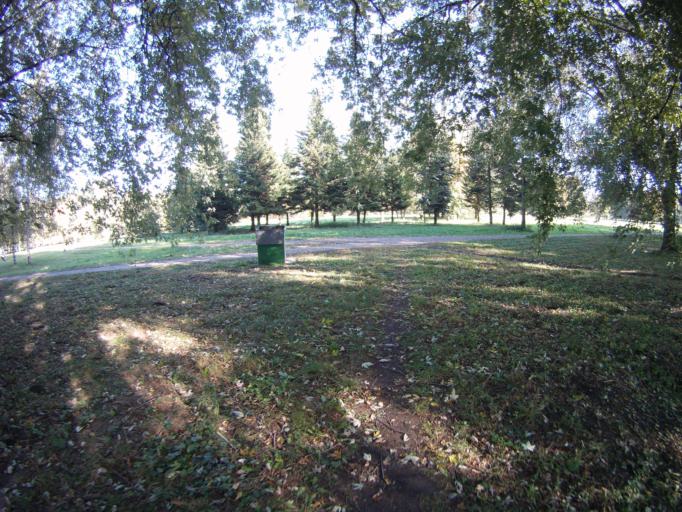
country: BY
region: Minsk
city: Minsk
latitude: 53.9379
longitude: 27.5672
